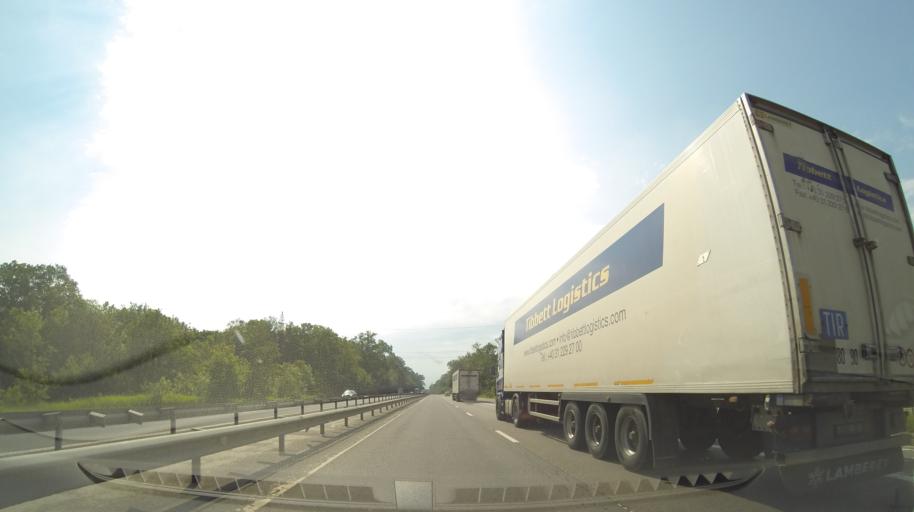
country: RO
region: Giurgiu
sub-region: Comuna Vanatorii Mici
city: Vanatorii Mici
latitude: 44.5041
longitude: 25.5780
